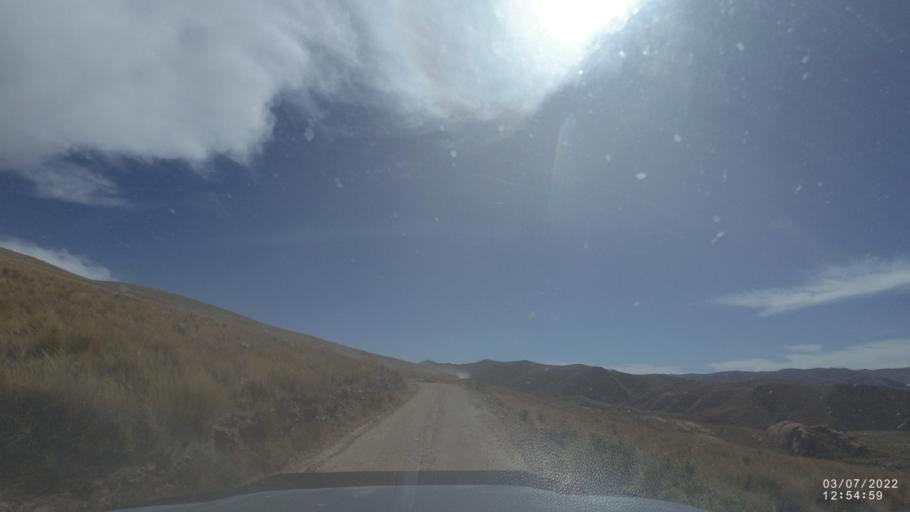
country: BO
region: Cochabamba
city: Irpa Irpa
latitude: -17.7359
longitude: -66.6682
